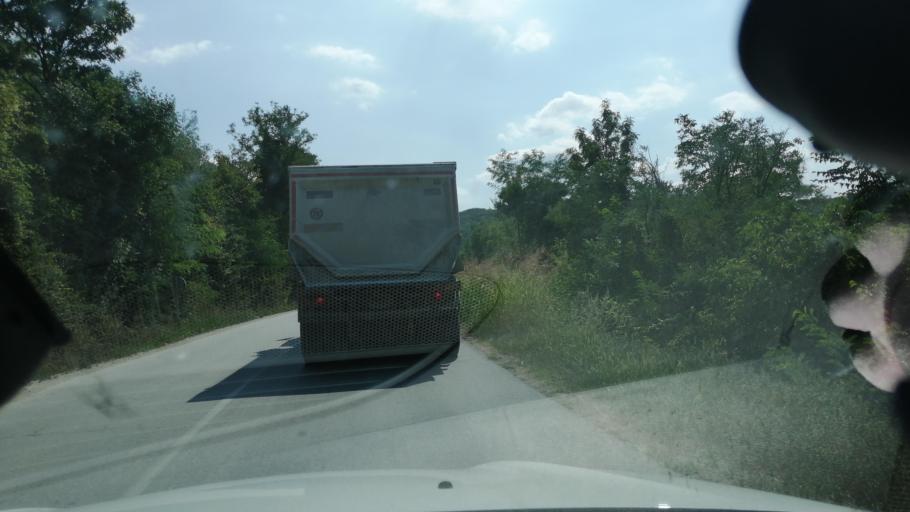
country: RS
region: Central Serbia
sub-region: Moravicki Okrug
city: Cacak
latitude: 43.8526
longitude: 20.3033
